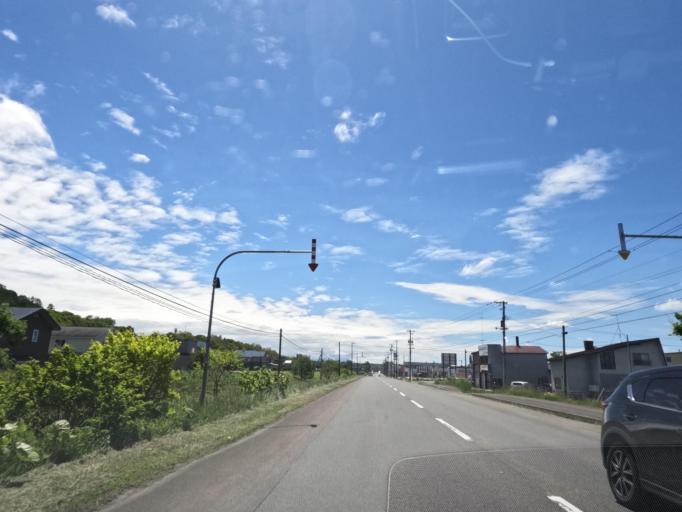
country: JP
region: Hokkaido
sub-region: Asahikawa-shi
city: Asahikawa
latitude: 43.6879
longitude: 142.3900
